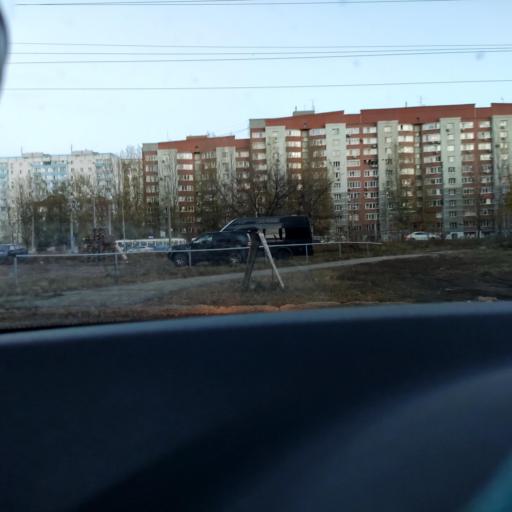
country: RU
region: Samara
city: Samara
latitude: 53.2677
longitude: 50.2196
